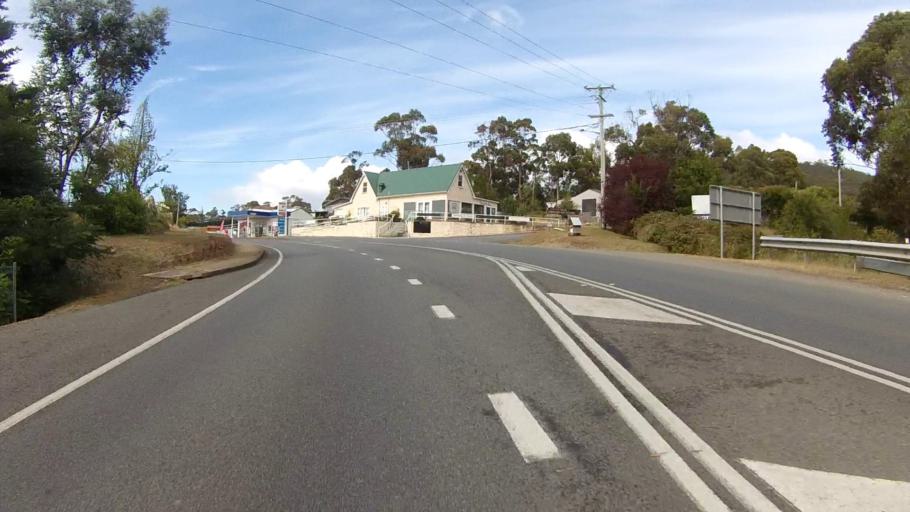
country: AU
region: Tasmania
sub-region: Kingborough
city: Kettering
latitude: -43.1226
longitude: 147.2454
